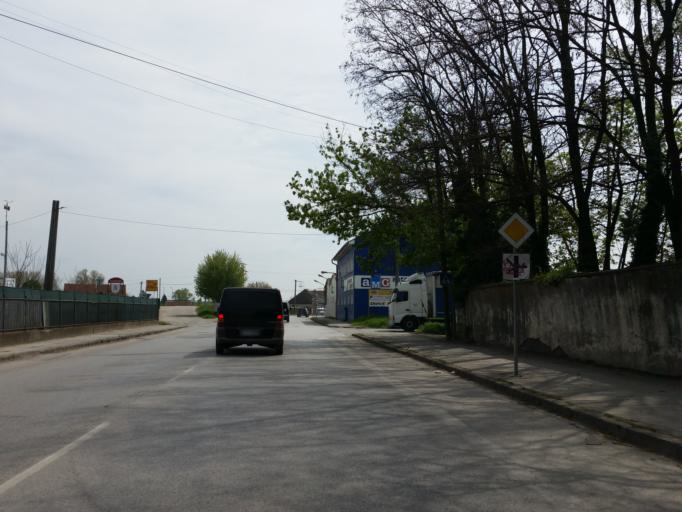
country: SK
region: Trnavsky
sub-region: Okres Galanta
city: Galanta
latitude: 48.2767
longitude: 17.7424
